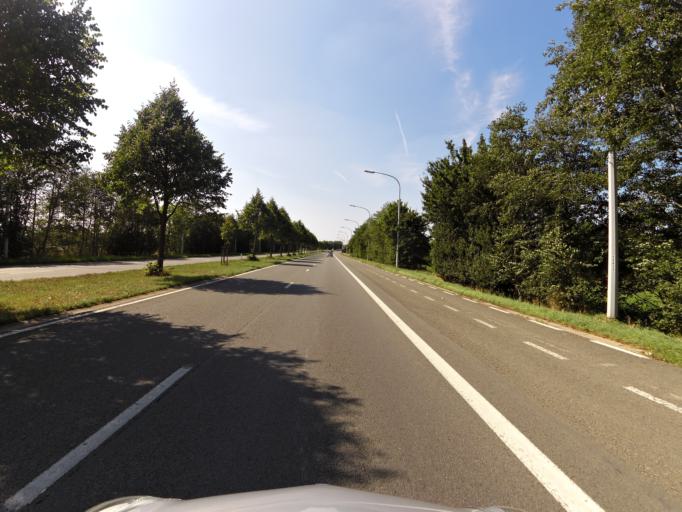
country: BE
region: Flanders
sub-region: Provincie Oost-Vlaanderen
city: Deinze
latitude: 50.9892
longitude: 3.5155
